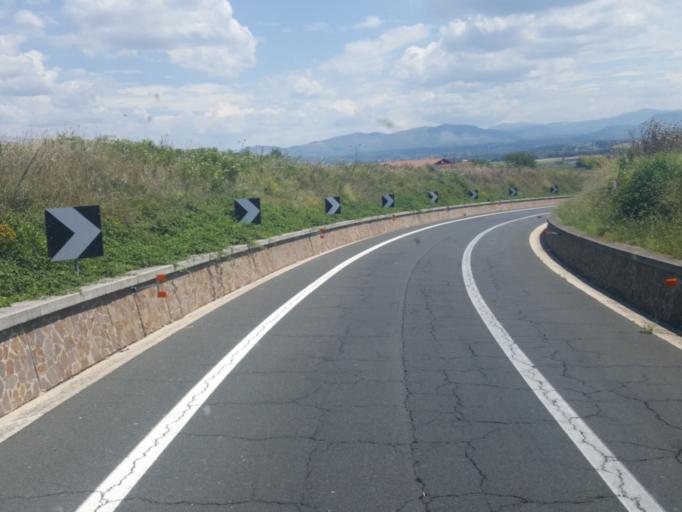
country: IT
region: Latium
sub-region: Citta metropolitana di Roma Capitale
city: Fiano Romano
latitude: 42.1409
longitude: 12.6082
